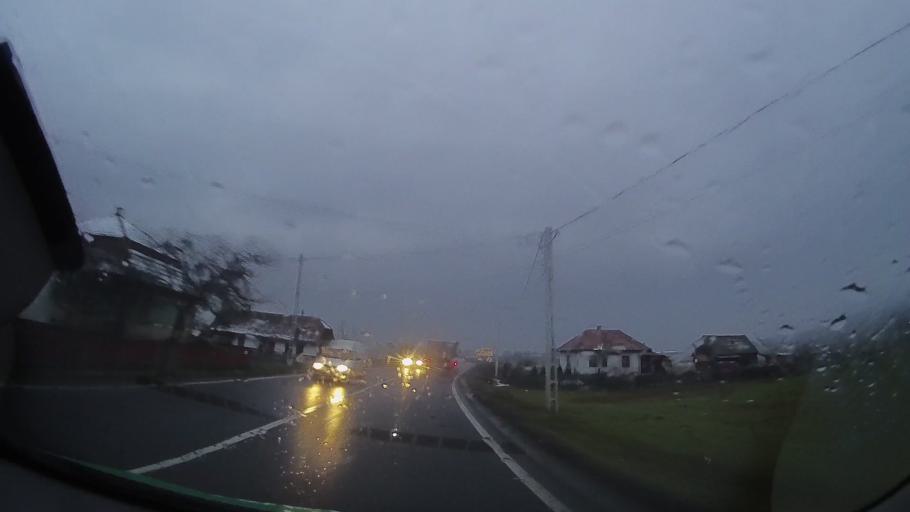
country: RO
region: Harghita
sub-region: Comuna Lazarea
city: Lazarea
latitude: 46.7582
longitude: 25.5167
